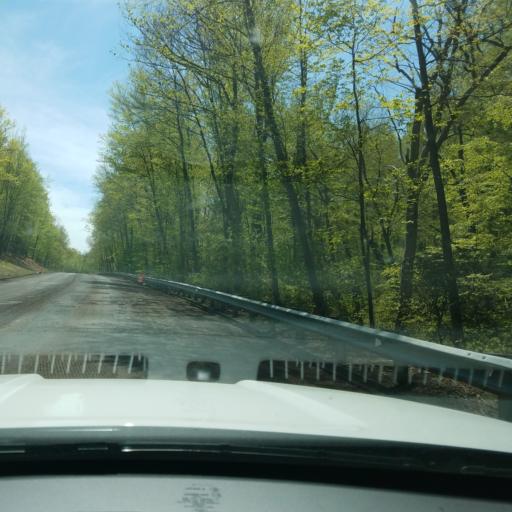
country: US
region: Connecticut
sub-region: Middlesex County
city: Higganum
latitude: 41.5197
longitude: -72.5715
